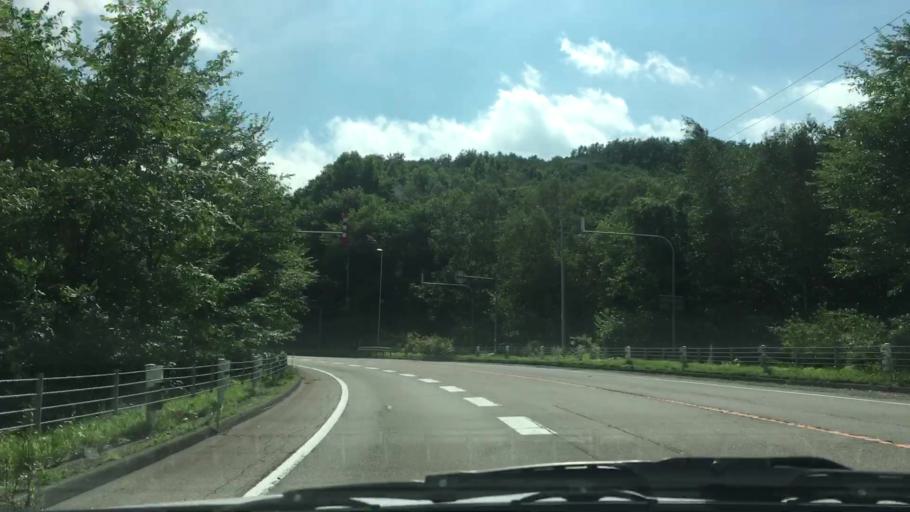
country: JP
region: Hokkaido
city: Otofuke
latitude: 43.2828
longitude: 143.4066
